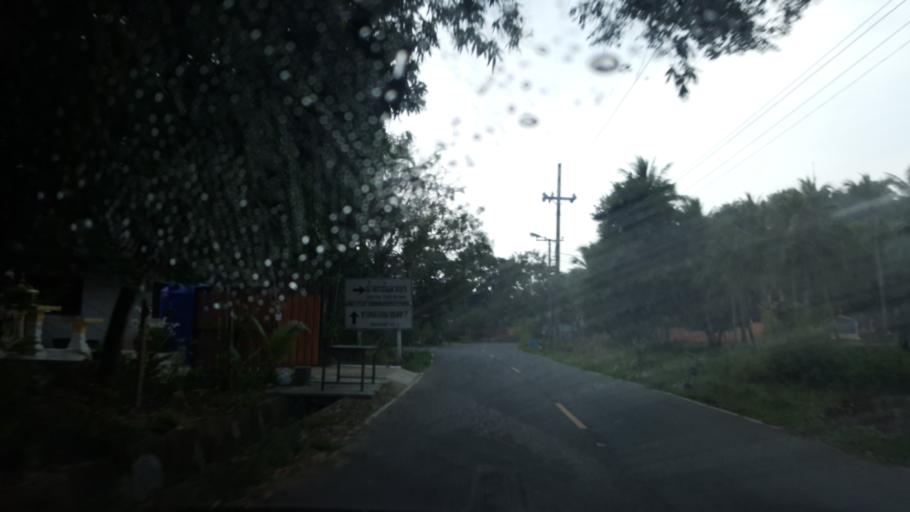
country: TH
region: Chon Buri
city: Ban Bueng
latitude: 13.2353
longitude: 101.0300
